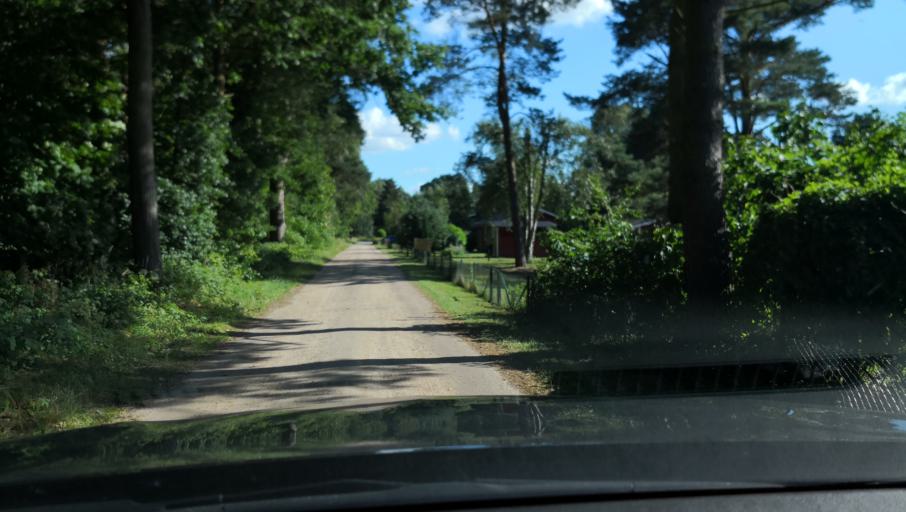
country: SE
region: Skane
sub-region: Kristianstads Kommun
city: Degeberga
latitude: 55.7916
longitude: 14.1953
